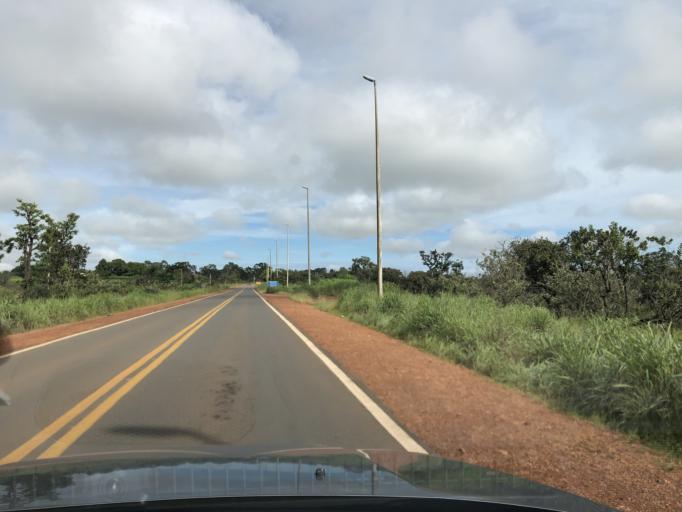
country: BR
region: Federal District
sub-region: Brasilia
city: Brasilia
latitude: -15.7335
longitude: -48.0790
